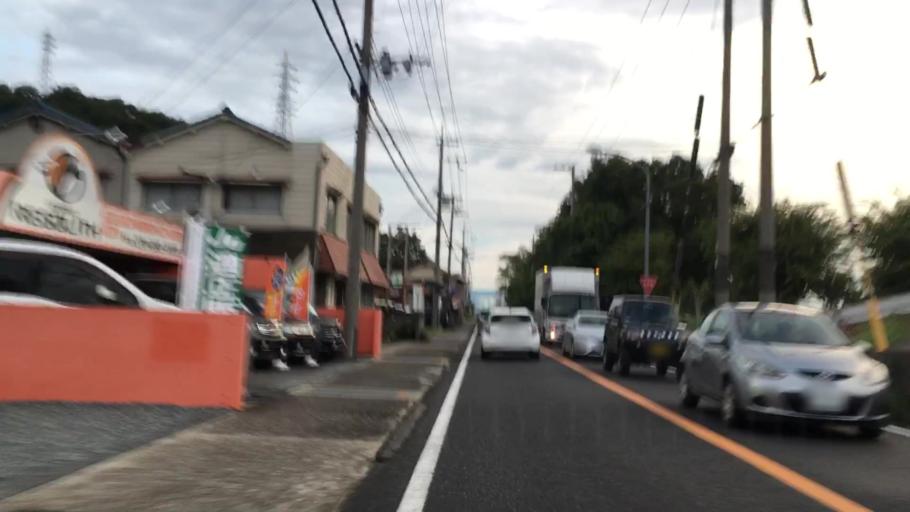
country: JP
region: Hyogo
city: Himeji
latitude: 34.8885
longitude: 134.7300
